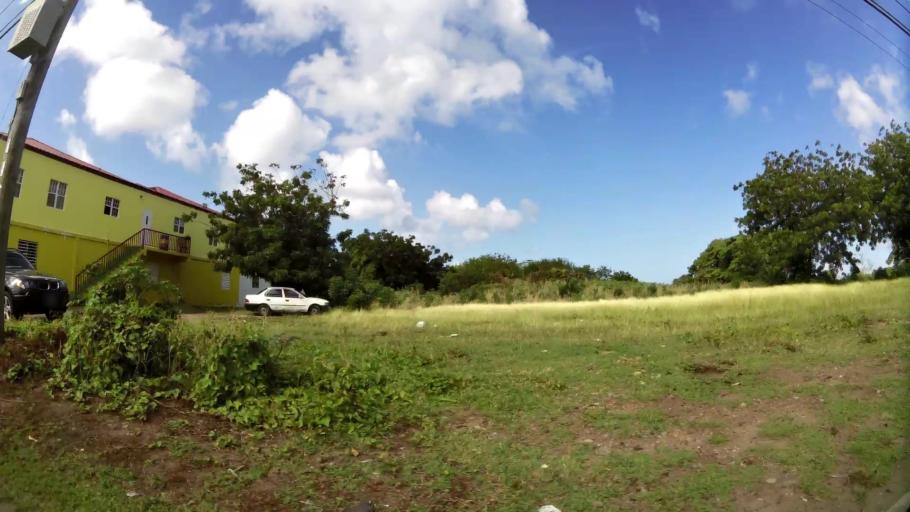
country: KN
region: Saint Paul Charlestown
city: Charlestown
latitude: 17.1324
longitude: -62.6186
